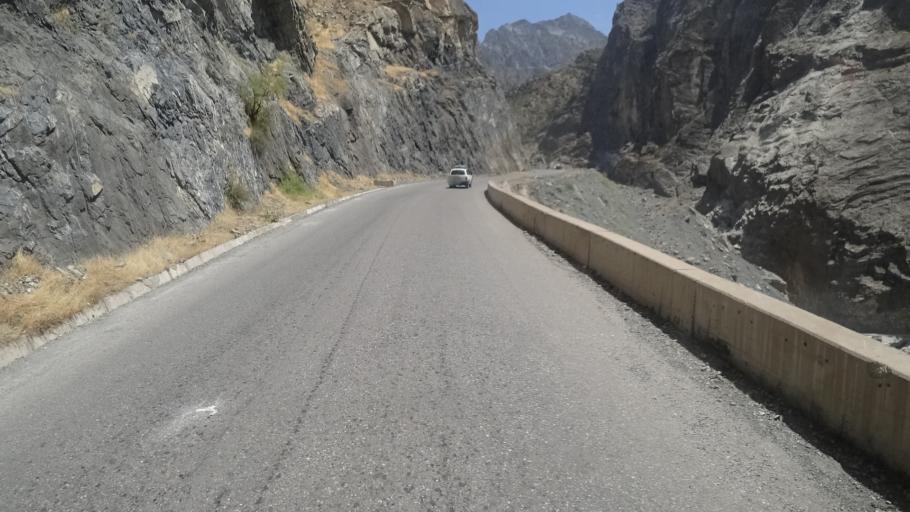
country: AF
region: Badakhshan
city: Deh Khwahan
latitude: 38.0003
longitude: 70.3204
